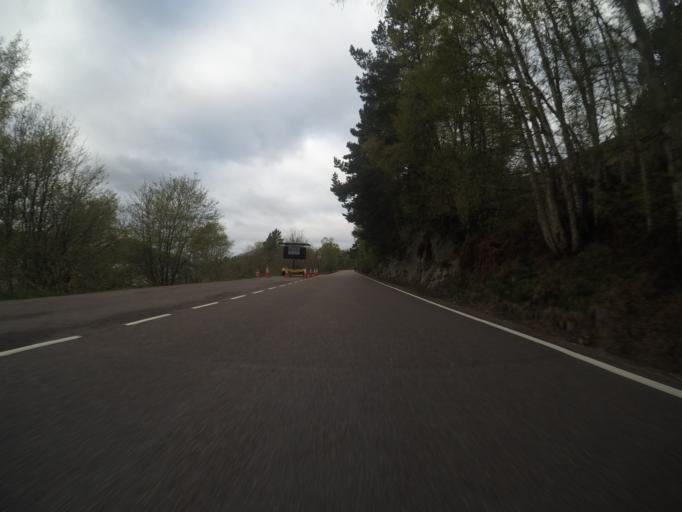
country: GB
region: Scotland
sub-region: Highland
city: Kingussie
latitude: 56.9745
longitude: -4.4148
